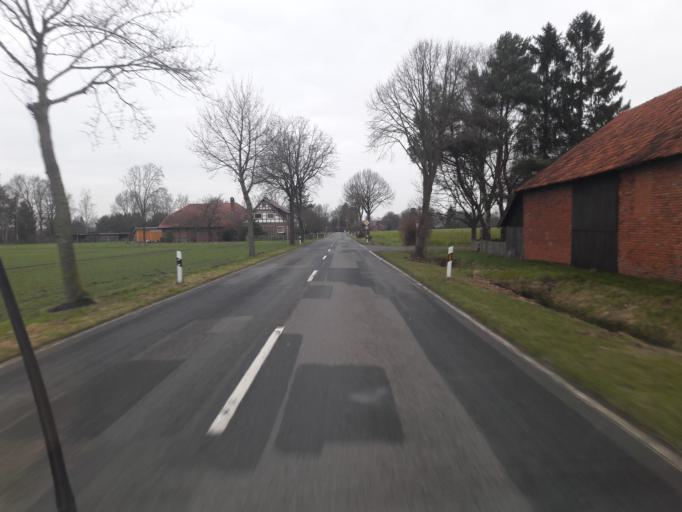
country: DE
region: Lower Saxony
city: Warmsen
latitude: 52.4195
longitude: 8.8573
